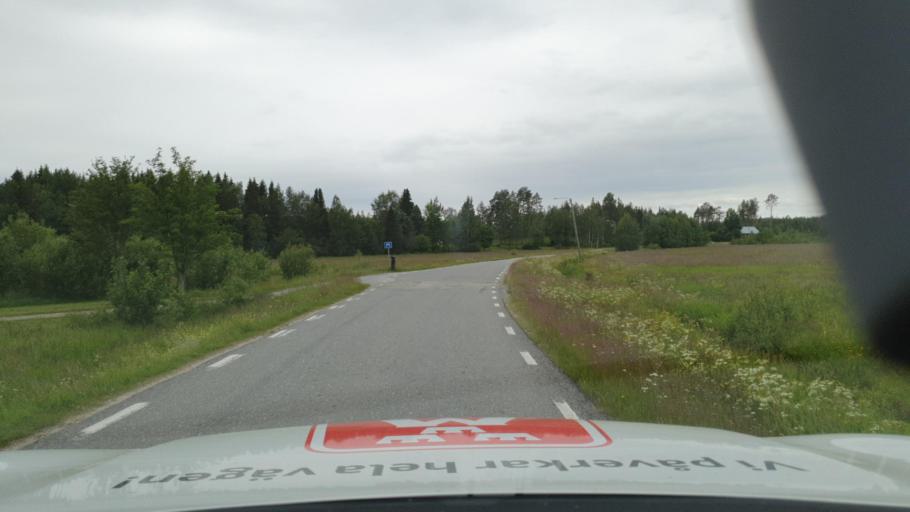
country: SE
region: Vaesterbotten
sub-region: Nordmalings Kommun
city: Nordmaling
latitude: 63.4994
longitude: 19.4206
